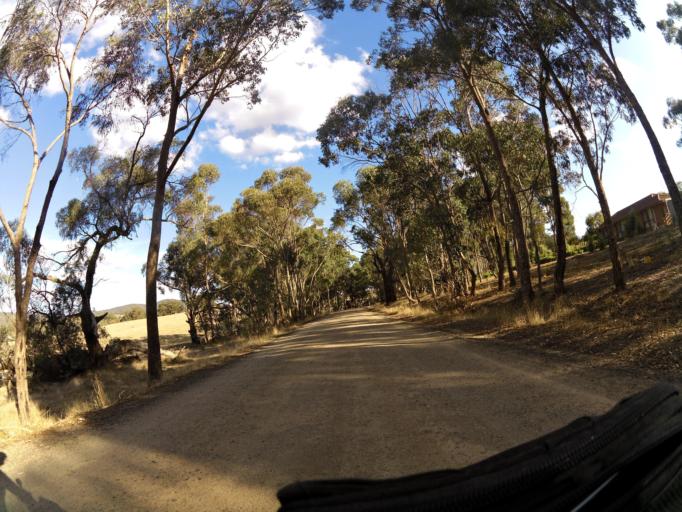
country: AU
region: Victoria
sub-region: Greater Bendigo
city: Kennington
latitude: -37.0162
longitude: 144.8075
